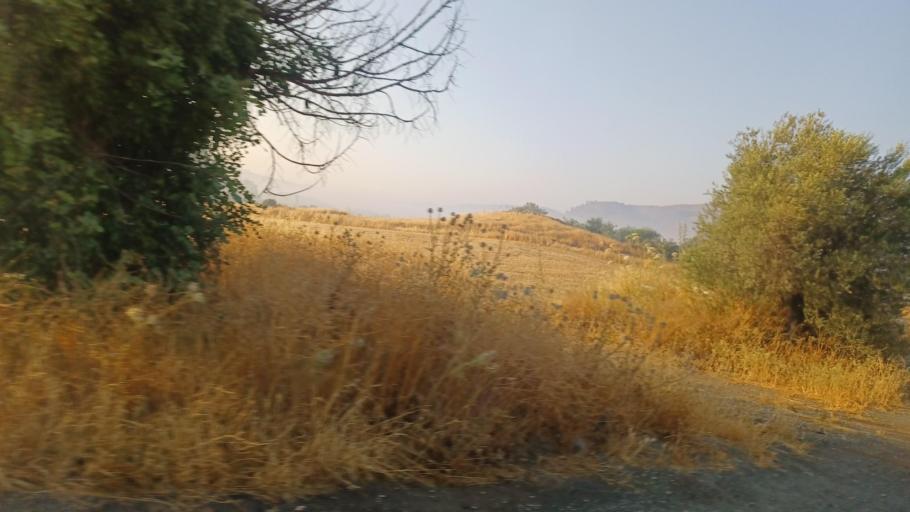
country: CY
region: Larnaka
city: Mosfiloti
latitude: 34.9723
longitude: 33.4398
